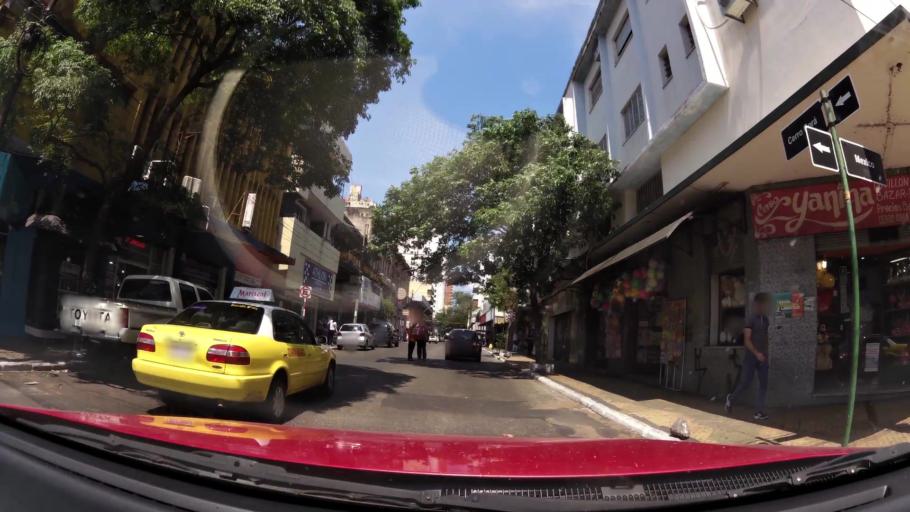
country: PY
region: Asuncion
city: Asuncion
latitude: -25.2857
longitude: -57.6316
